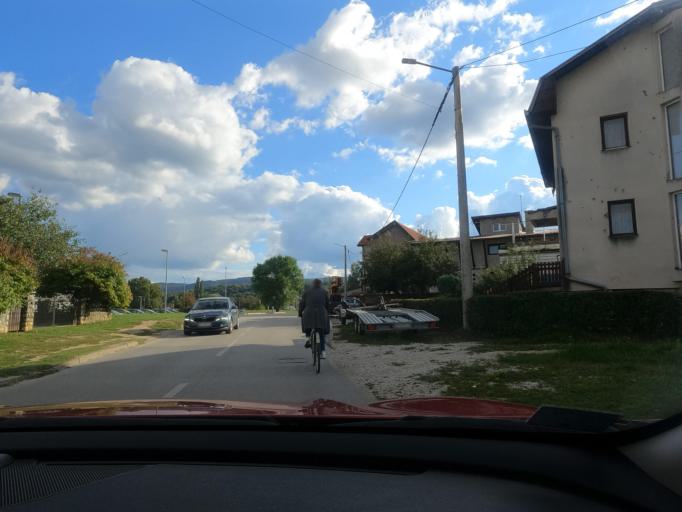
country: HR
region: Sisacko-Moslavacka
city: Petrinja
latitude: 45.4389
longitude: 16.2712
